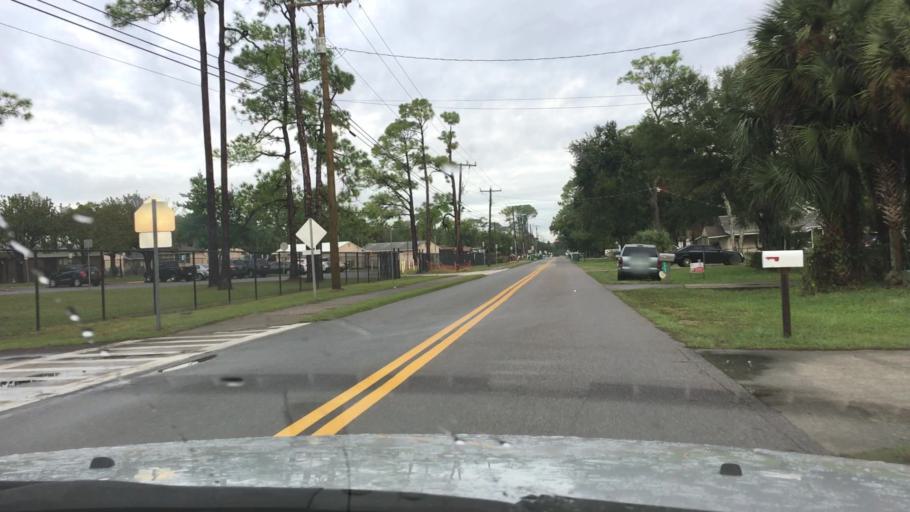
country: US
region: Florida
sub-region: Volusia County
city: Holly Hill
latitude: 29.2491
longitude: -81.0540
